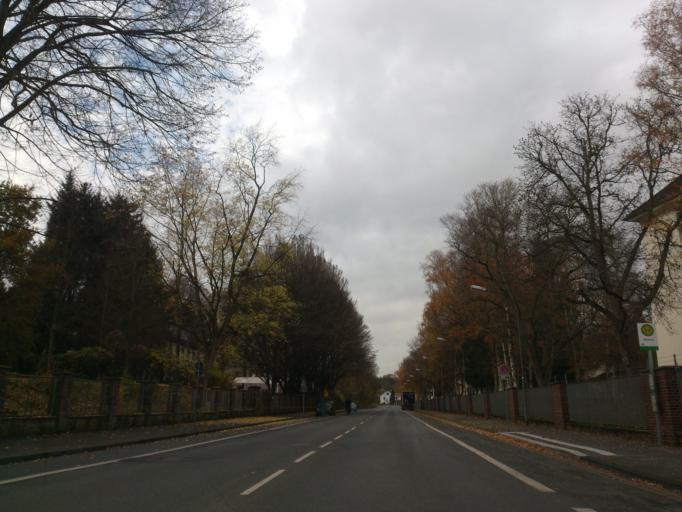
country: DE
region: North Rhine-Westphalia
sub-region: Regierungsbezirk Detmold
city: Hoexter
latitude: 51.7806
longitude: 9.3759
